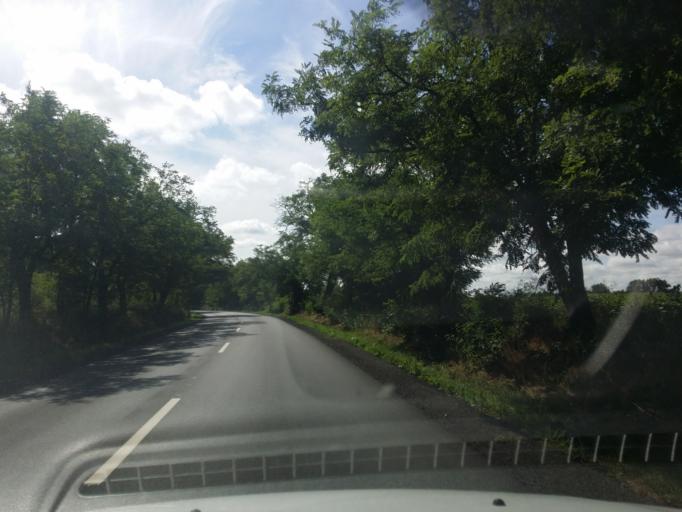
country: HU
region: Heves
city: Heves
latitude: 47.6268
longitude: 20.2379
